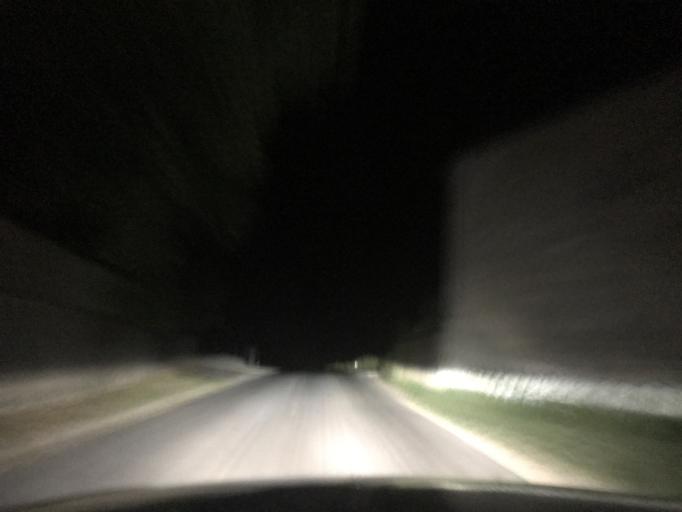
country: DE
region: Bavaria
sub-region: Upper Palatinate
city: Auerbach
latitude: 49.7097
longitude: 11.5962
